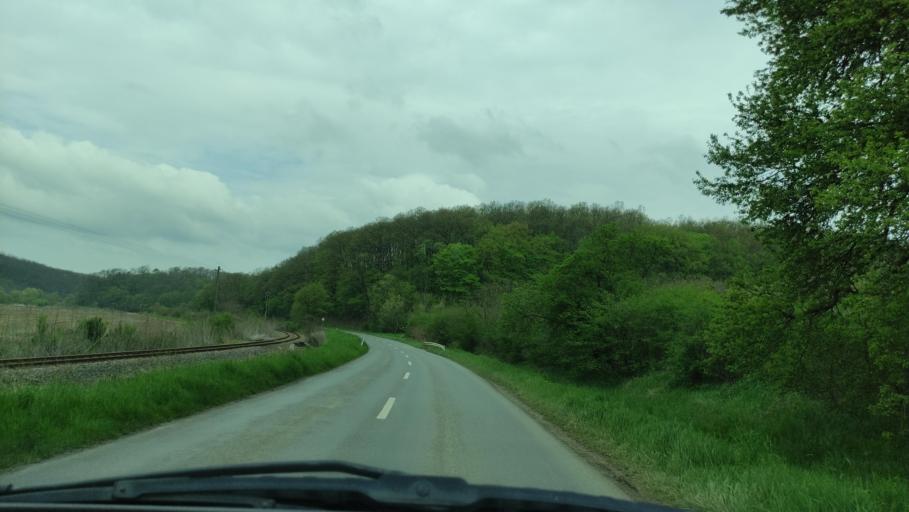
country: HU
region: Baranya
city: Komlo
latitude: 46.2261
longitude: 18.2328
